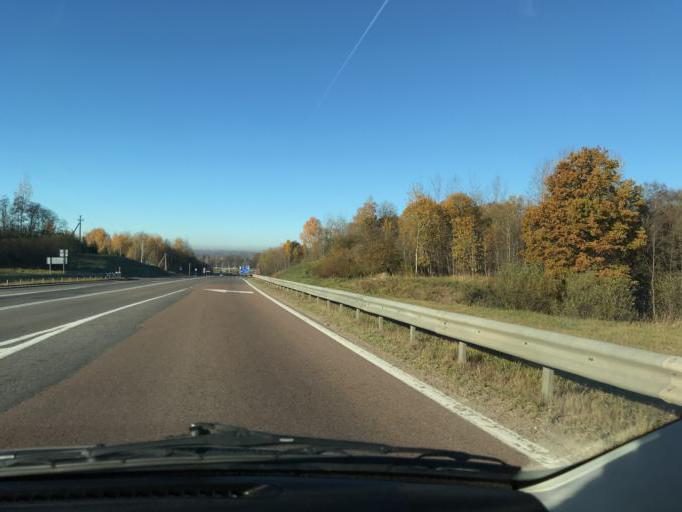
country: BY
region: Vitebsk
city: Vitebsk
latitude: 55.1035
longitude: 30.2955
